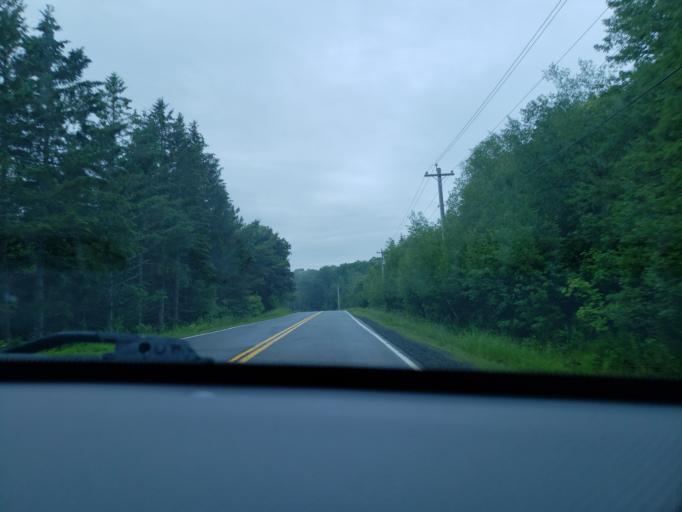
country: CA
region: Nova Scotia
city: Windsor
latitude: 45.0605
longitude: -63.9840
